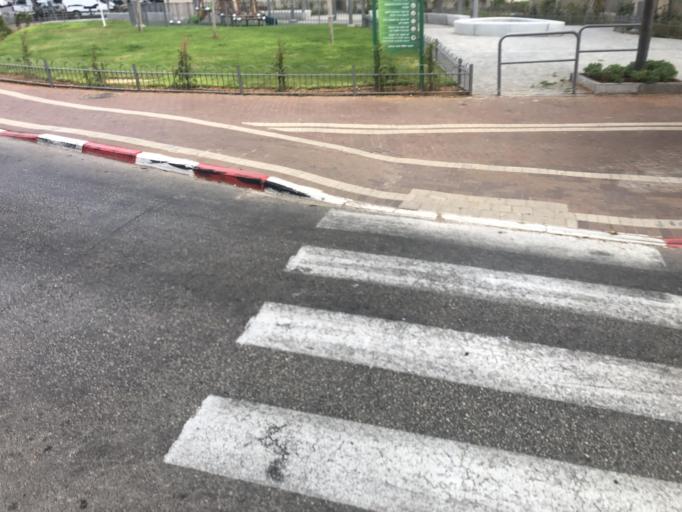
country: IL
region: Central District
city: Yehud
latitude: 32.0282
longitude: 34.8895
